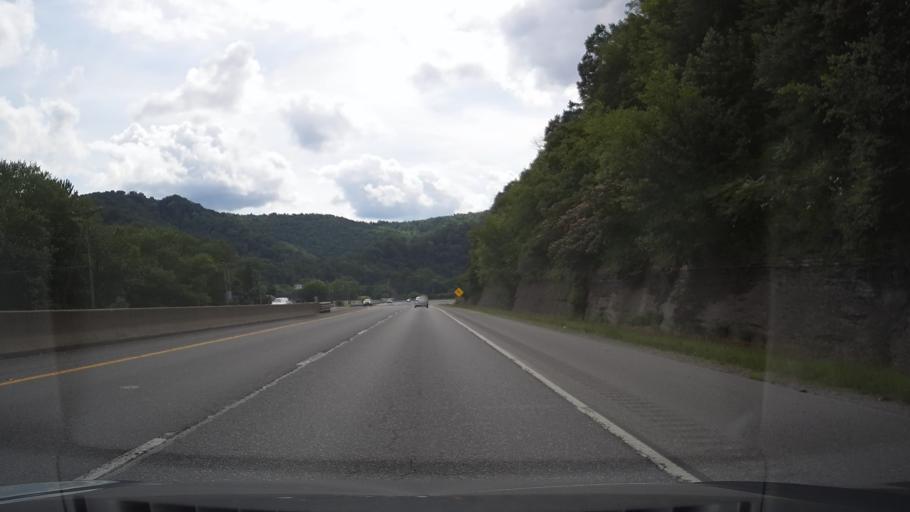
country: US
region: Kentucky
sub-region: Pike County
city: Coal Run Village
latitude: 37.5751
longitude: -82.6520
